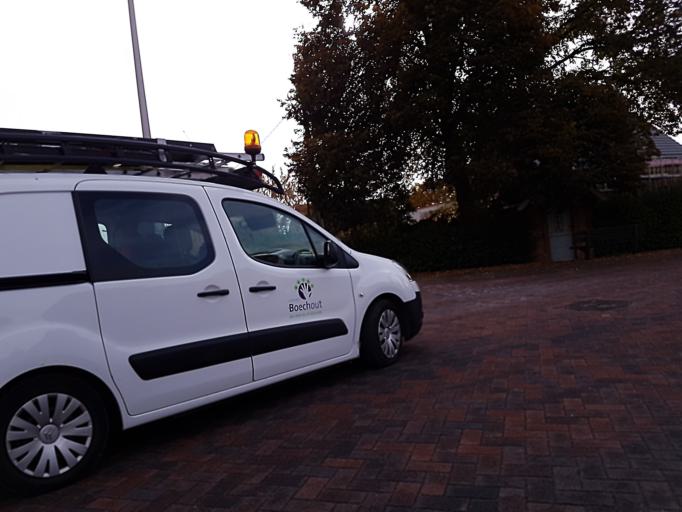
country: BE
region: Flanders
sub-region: Provincie Antwerpen
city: Wommelgem
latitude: 51.1734
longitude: 4.5275
